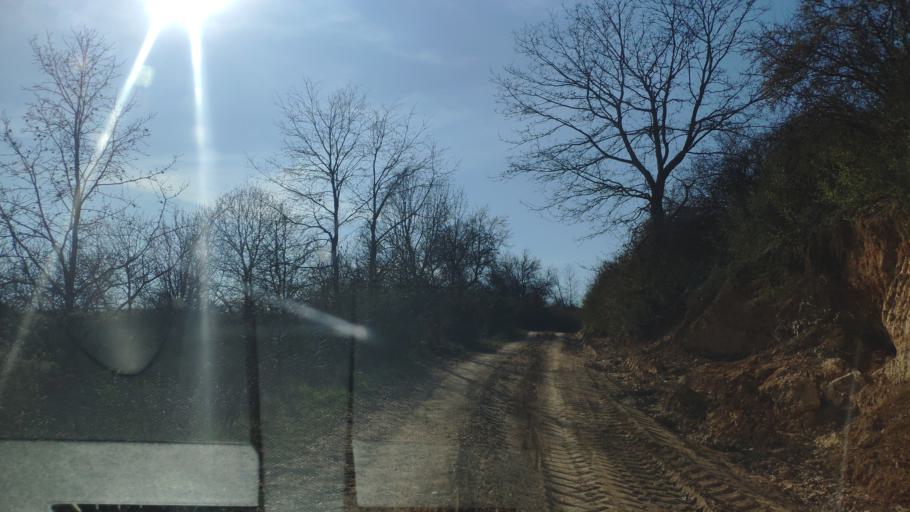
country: SK
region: Banskobystricky
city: Revuca
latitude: 48.5466
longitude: 20.2849
